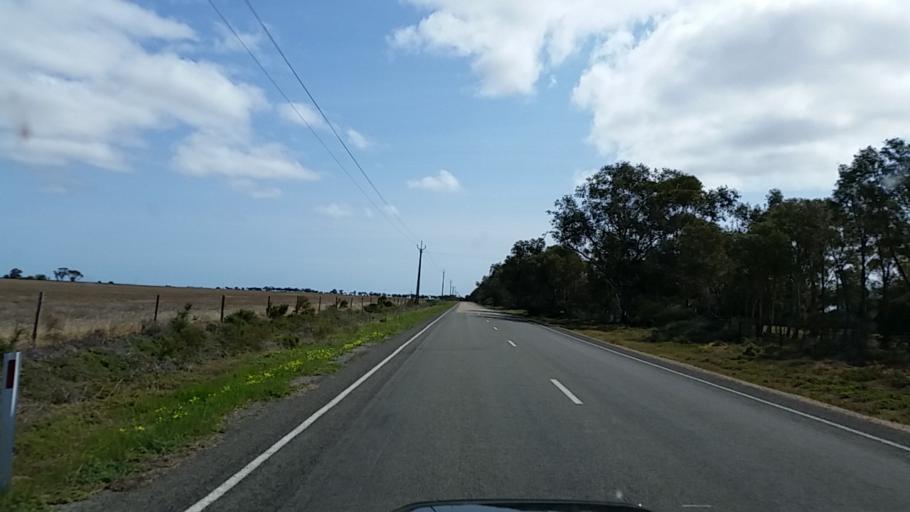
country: AU
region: South Australia
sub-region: Port Pirie City and Dists
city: Solomontown
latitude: -33.2301
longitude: 138.0225
